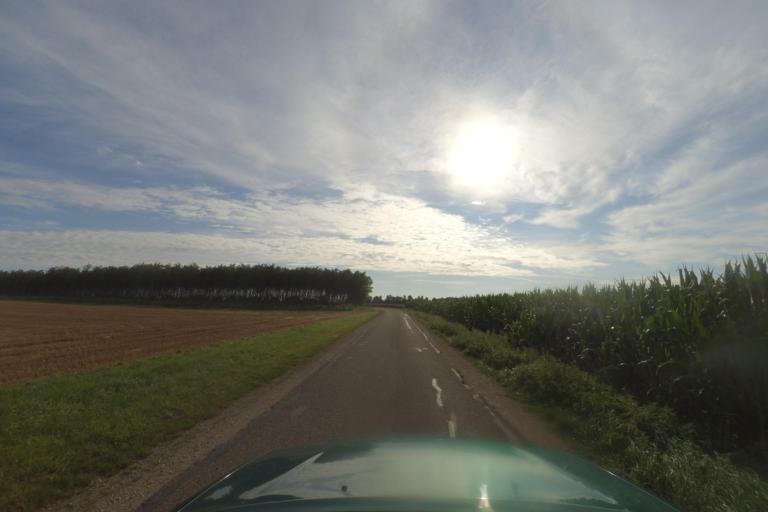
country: DE
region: Bavaria
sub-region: Upper Bavaria
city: Denkendorf
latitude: 48.9870
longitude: 11.5088
